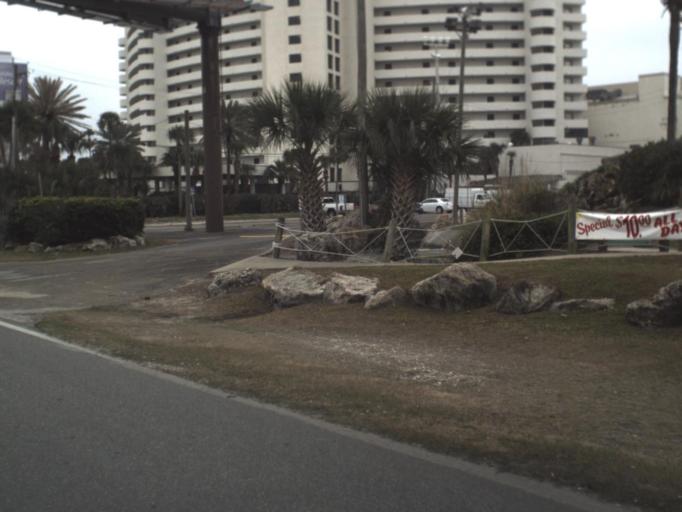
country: US
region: Florida
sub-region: Bay County
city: Panama City Beach
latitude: 30.1842
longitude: -85.8179
